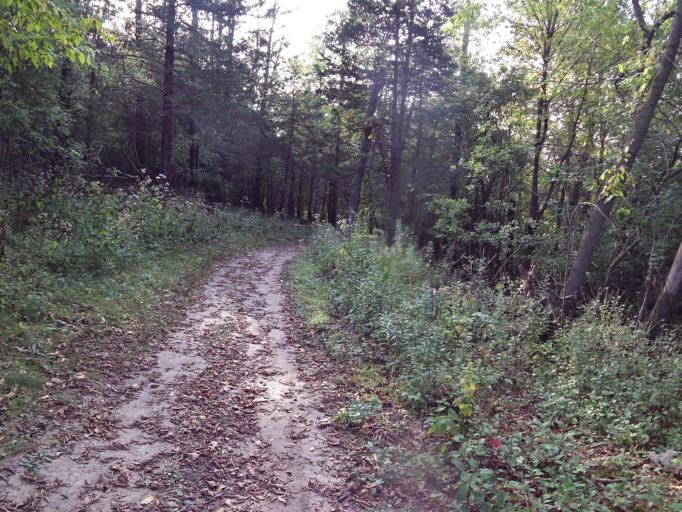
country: US
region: Minnesota
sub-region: Washington County
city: Afton
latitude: 44.8659
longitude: -92.7936
